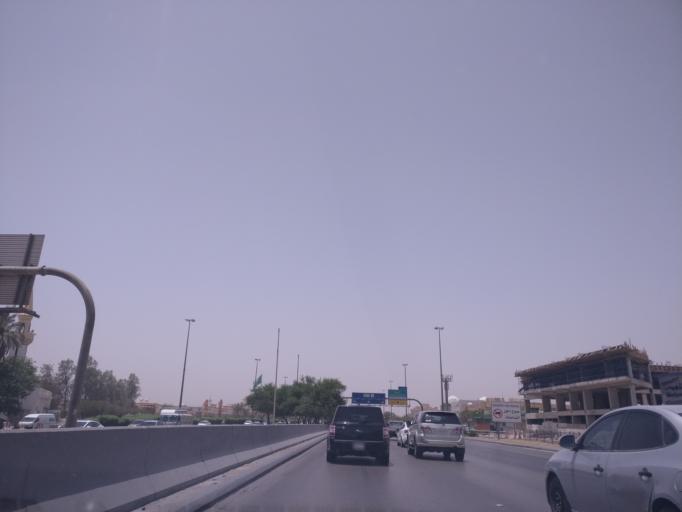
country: SA
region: Ar Riyad
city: Riyadh
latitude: 24.6098
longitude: 46.7071
